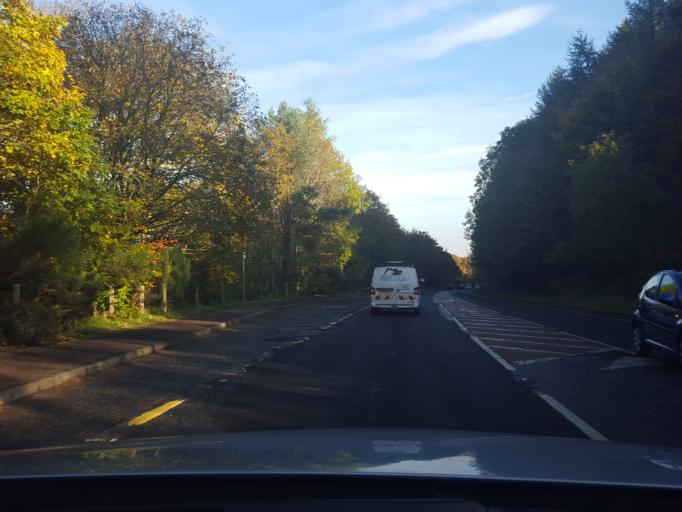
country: GB
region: Scotland
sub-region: Highland
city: Inverness
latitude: 57.4582
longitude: -4.2680
